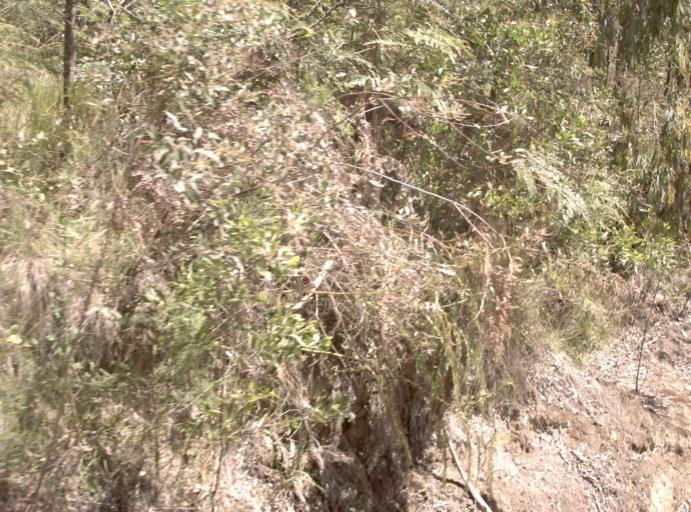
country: AU
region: Victoria
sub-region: East Gippsland
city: Lakes Entrance
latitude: -37.2250
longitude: 148.2637
